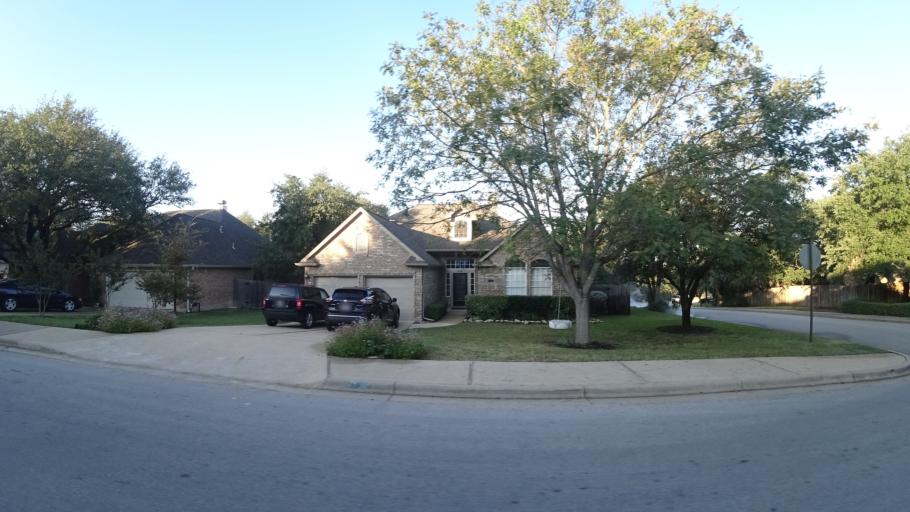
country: US
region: Texas
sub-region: Travis County
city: Hudson Bend
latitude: 30.3797
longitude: -97.8932
